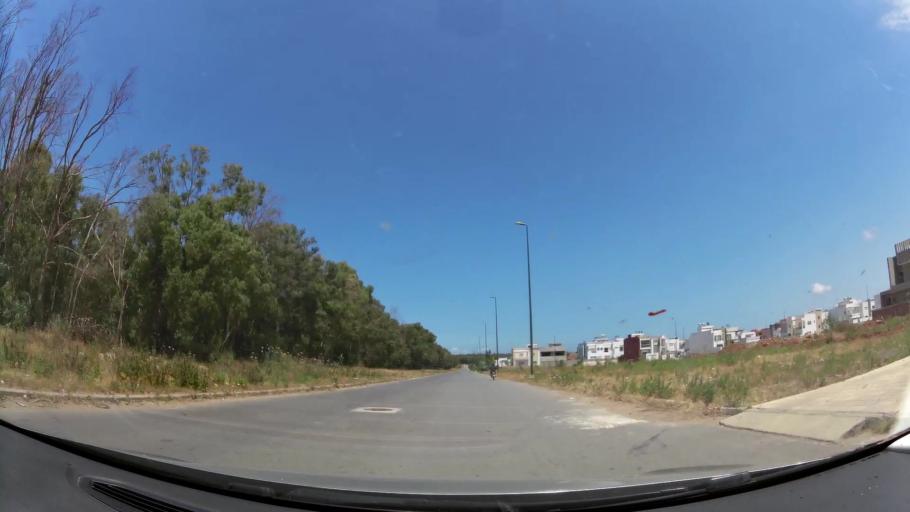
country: MA
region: Gharb-Chrarda-Beni Hssen
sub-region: Kenitra Province
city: Kenitra
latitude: 34.2644
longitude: -6.6308
